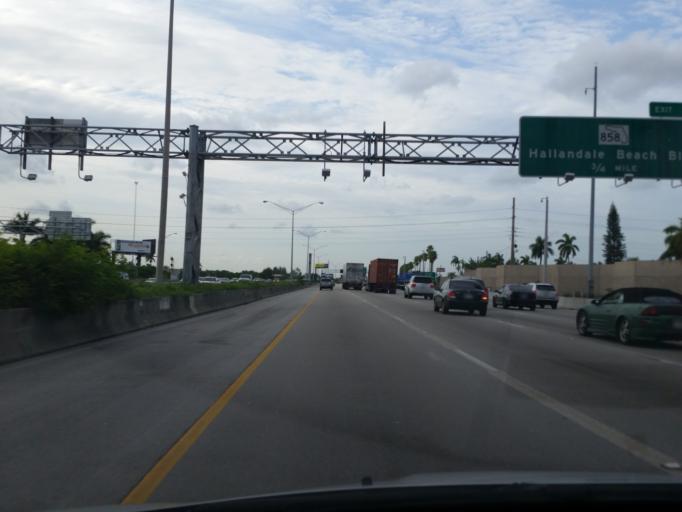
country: US
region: Florida
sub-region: Miami-Dade County
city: Ives Estates
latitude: 25.9723
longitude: -80.1657
